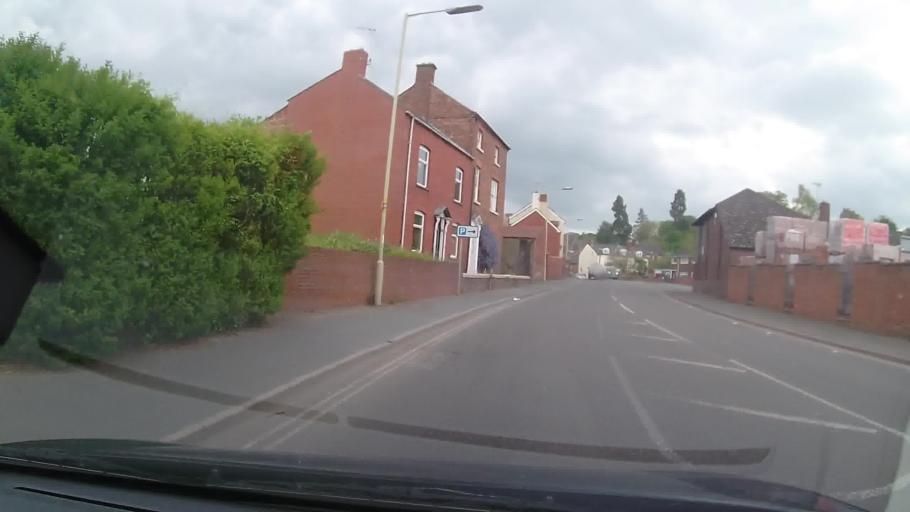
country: GB
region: England
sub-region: Shropshire
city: Ellesmere
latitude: 52.9092
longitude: -2.8926
